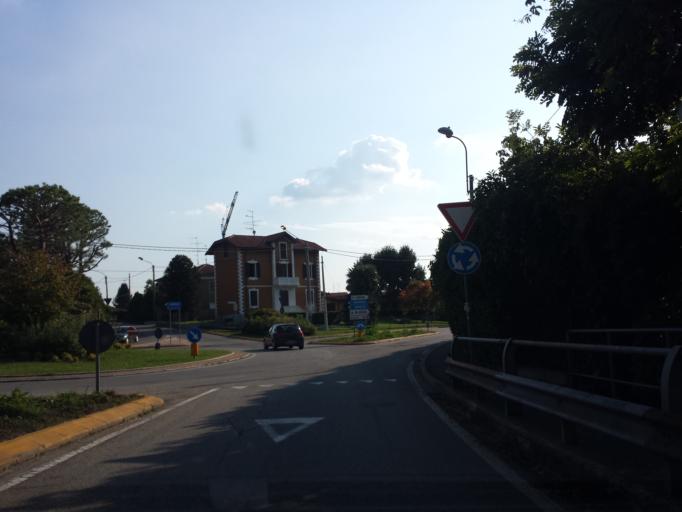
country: IT
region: Lombardy
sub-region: Provincia di Varese
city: Ispra
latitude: 45.8195
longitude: 8.6237
